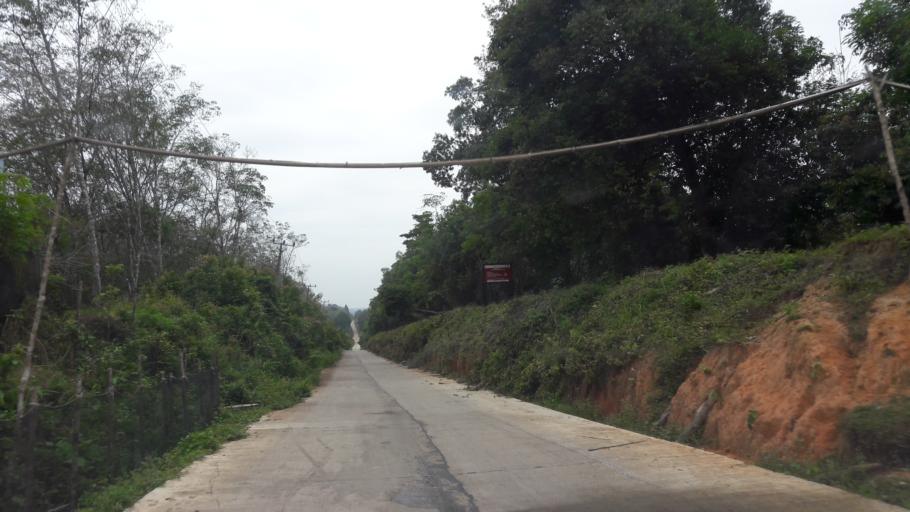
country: ID
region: South Sumatra
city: Gunungmenang
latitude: -3.2016
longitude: 103.8873
